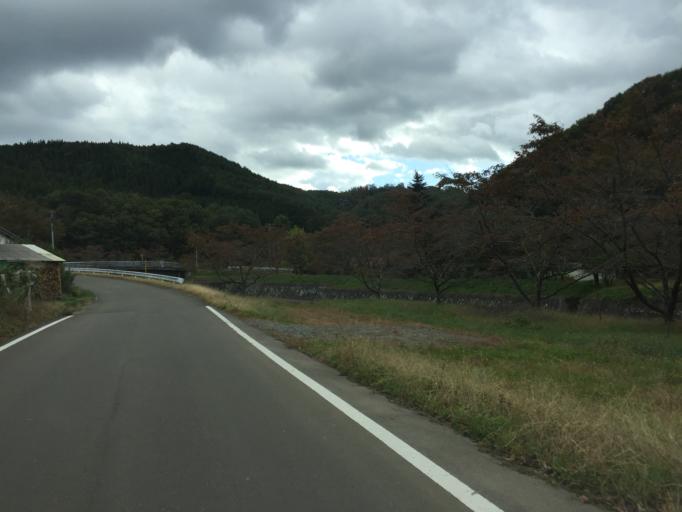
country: JP
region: Miyagi
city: Marumori
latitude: 37.7961
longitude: 140.7456
